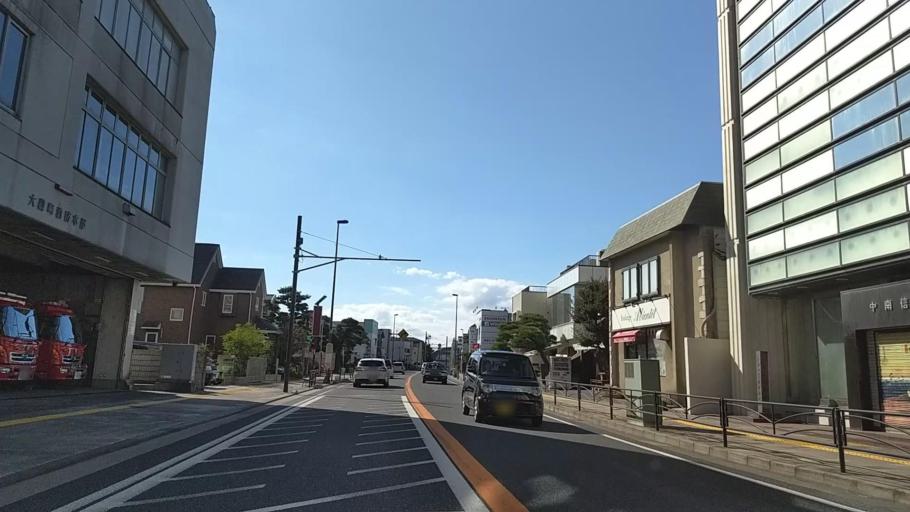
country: JP
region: Kanagawa
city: Oiso
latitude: 35.3088
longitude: 139.3152
